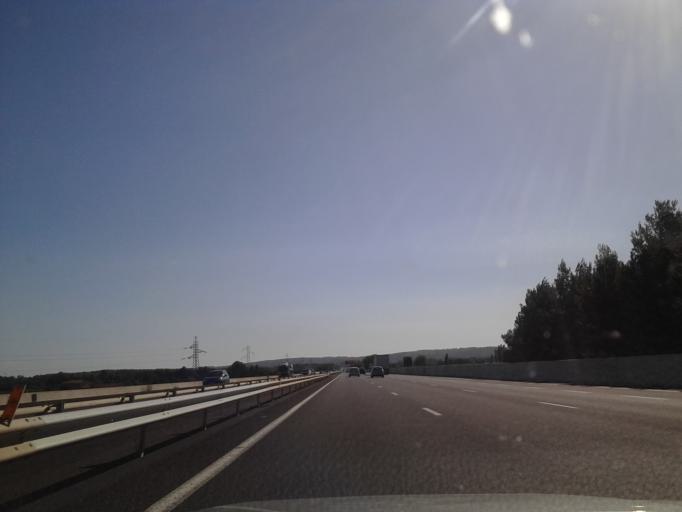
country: FR
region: Languedoc-Roussillon
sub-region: Departement de l'Aude
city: Narbonne
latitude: 43.1668
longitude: 3.0028
